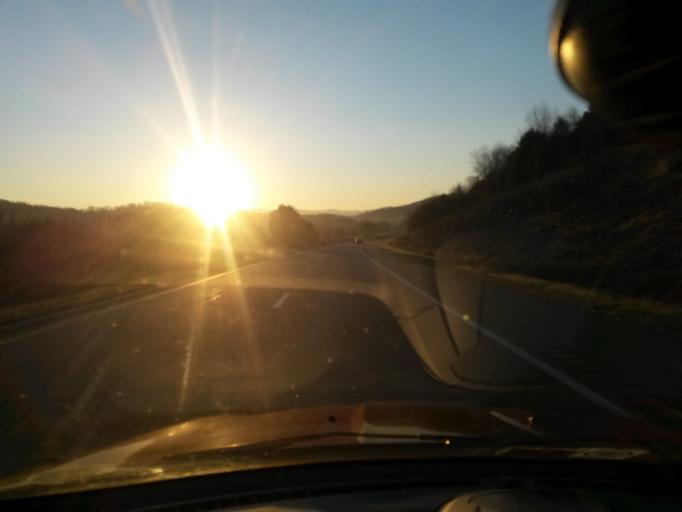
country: US
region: Virginia
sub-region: City of Lexington
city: Lexington
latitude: 37.8613
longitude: -79.4880
